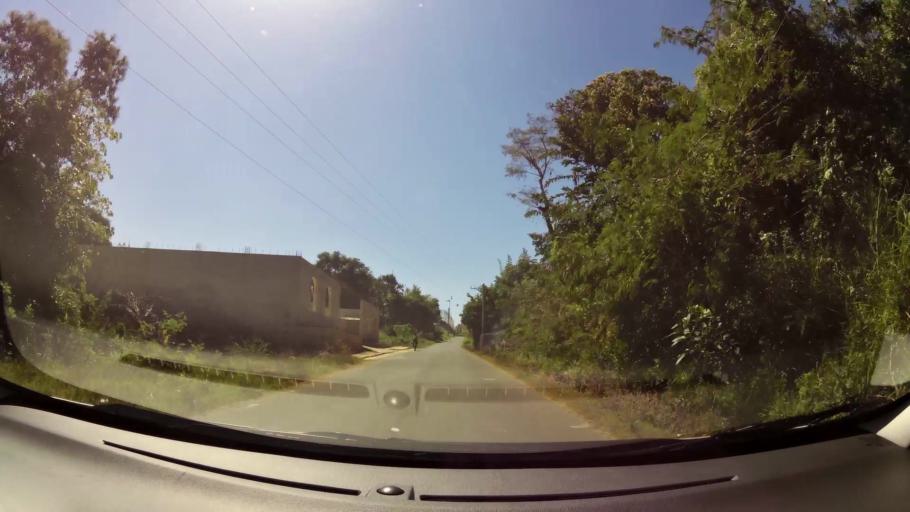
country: SV
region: Ahuachapan
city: Ahuachapan
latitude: 13.9334
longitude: -89.8408
